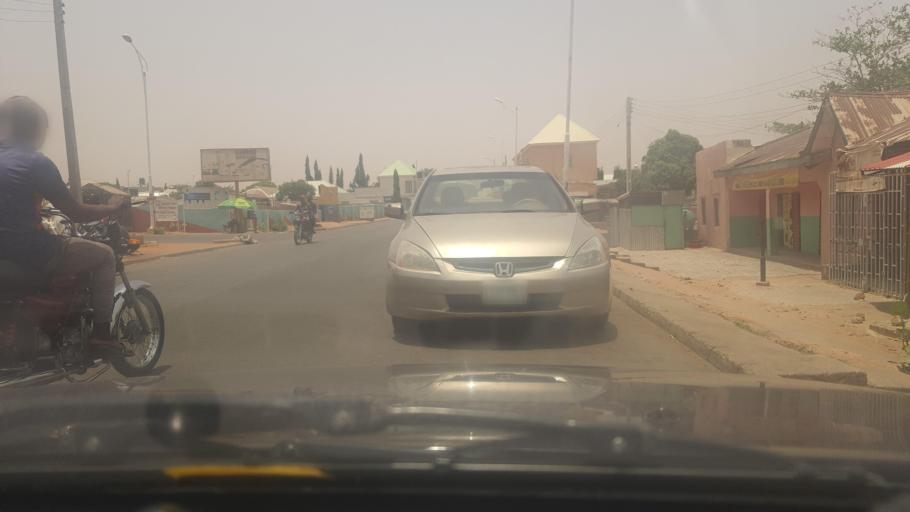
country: NG
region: Gombe
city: Gombe
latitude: 10.2990
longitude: 11.1465
